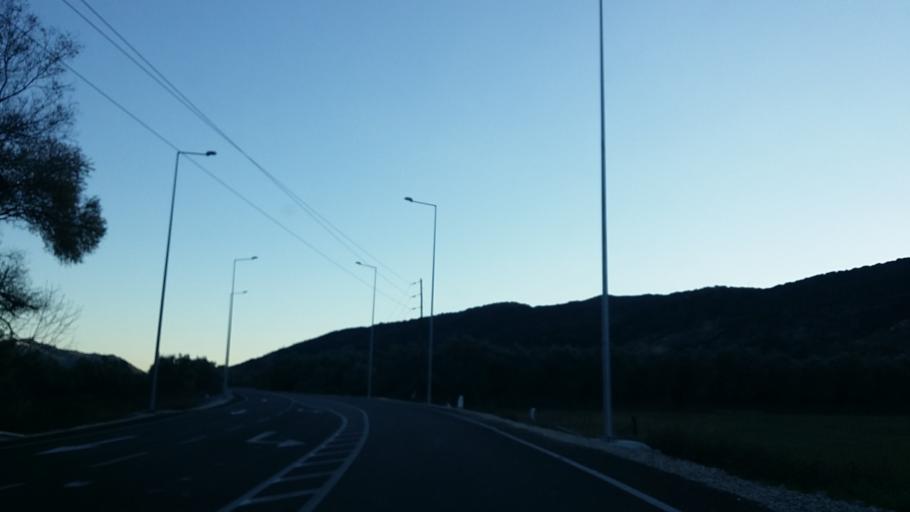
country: GR
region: West Greece
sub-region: Nomos Aitolias kai Akarnanias
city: Lepenou
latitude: 38.7302
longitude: 21.3344
